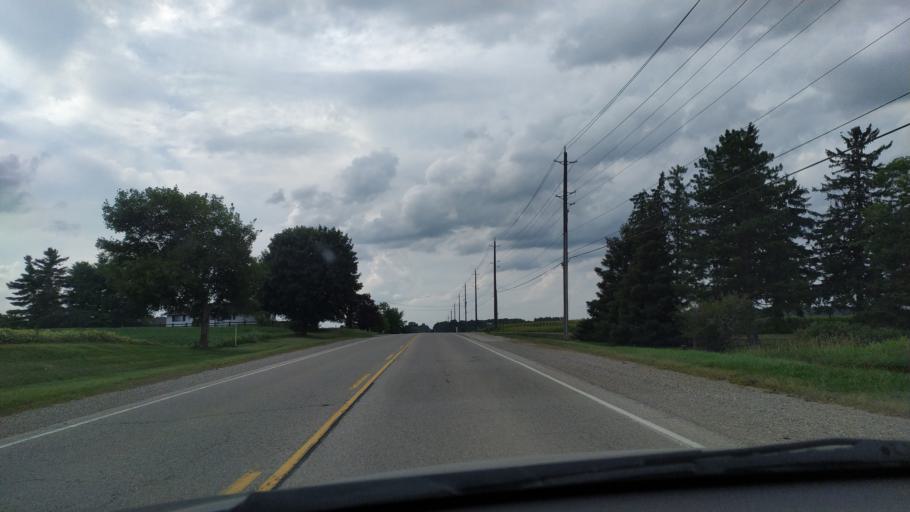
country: CA
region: Ontario
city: Kitchener
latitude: 43.3649
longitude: -80.5526
